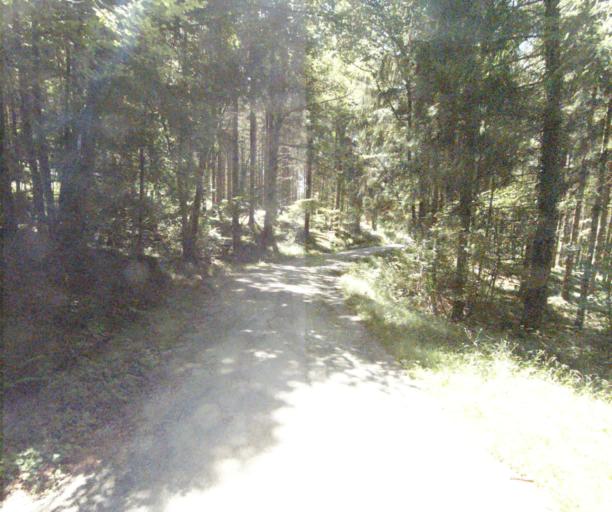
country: FR
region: Midi-Pyrenees
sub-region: Departement du Tarn
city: Dourgne
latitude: 43.4445
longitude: 2.2007
